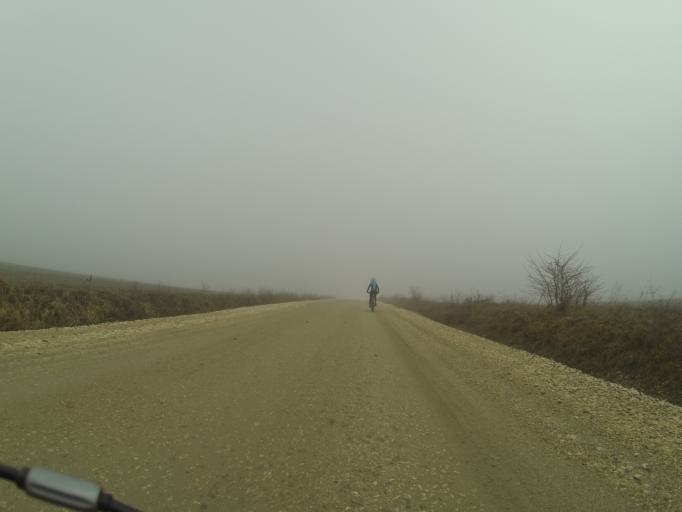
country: RO
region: Mehedinti
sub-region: Comuna Balacita
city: Gvardinita
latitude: 44.4283
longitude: 23.1312
